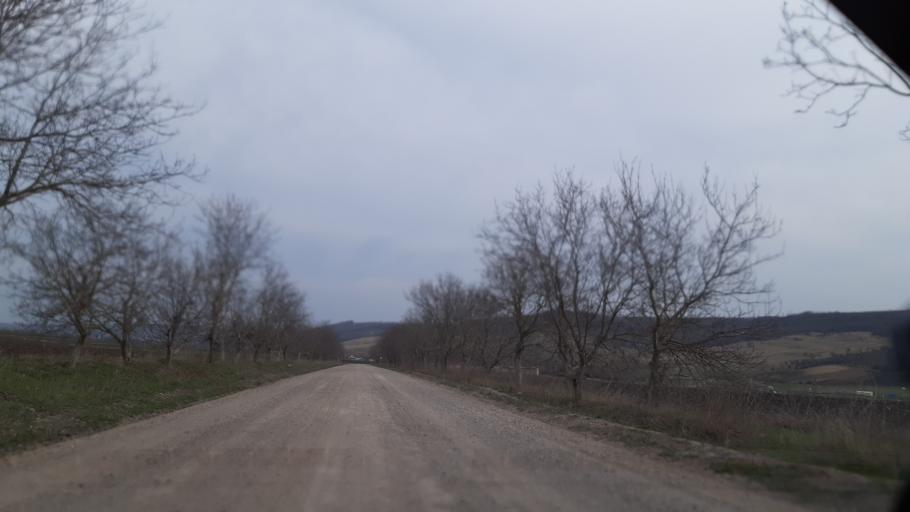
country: MD
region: Soldanesti
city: Soldanesti
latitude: 47.6907
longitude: 28.7406
